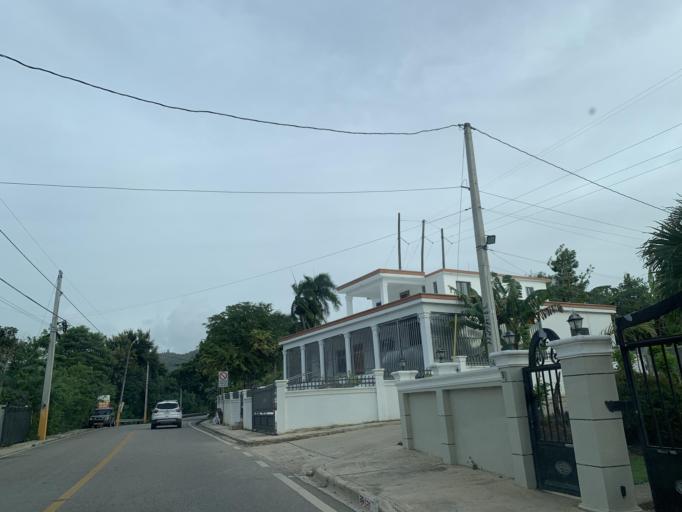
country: DO
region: Santiago
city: Pedro Garcia
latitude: 19.7005
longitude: -70.6240
